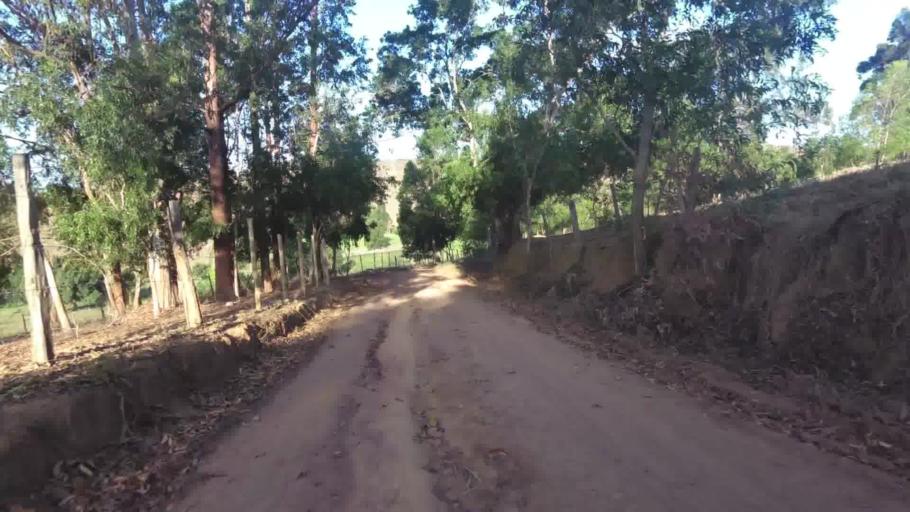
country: BR
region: Espirito Santo
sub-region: Marataizes
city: Marataizes
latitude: -21.1643
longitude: -41.0540
